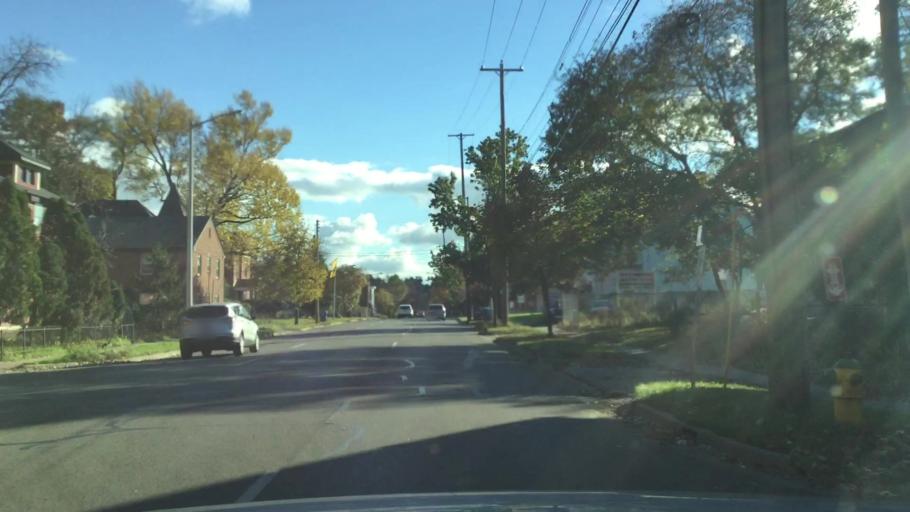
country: US
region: Michigan
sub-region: Kalamazoo County
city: Kalamazoo
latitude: 42.2807
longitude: -85.5896
